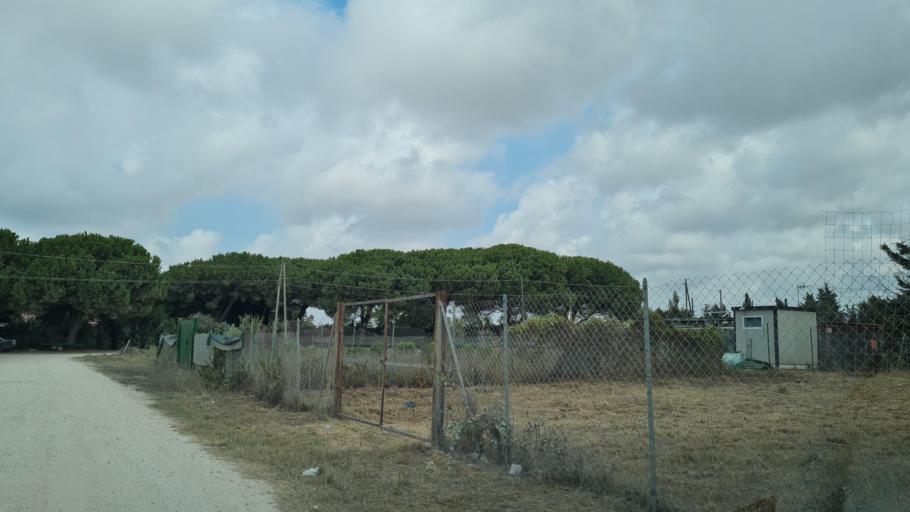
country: IT
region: Latium
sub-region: Provincia di Viterbo
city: Tarquinia
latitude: 42.1938
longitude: 11.7292
